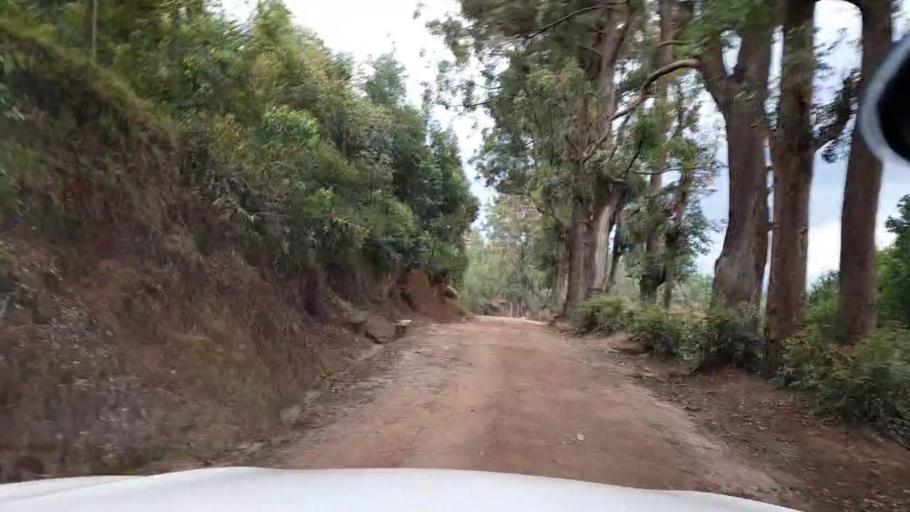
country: BI
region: Kayanza
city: Kayanza
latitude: -2.7945
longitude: 29.5166
